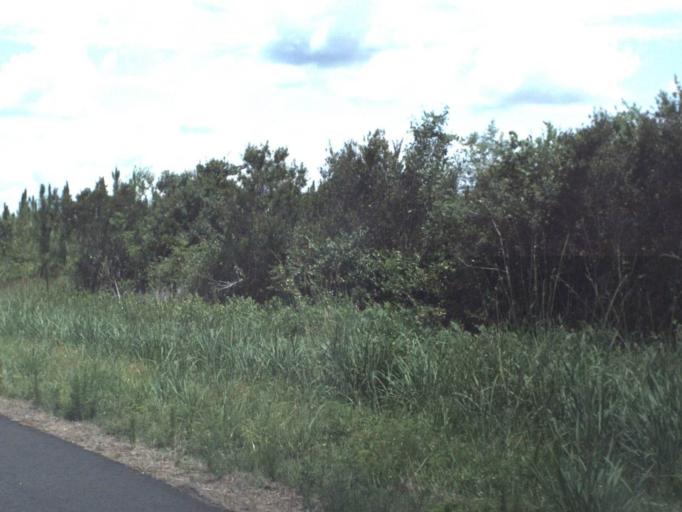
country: US
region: Florida
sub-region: Baker County
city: Macclenny
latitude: 30.5343
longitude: -82.3204
